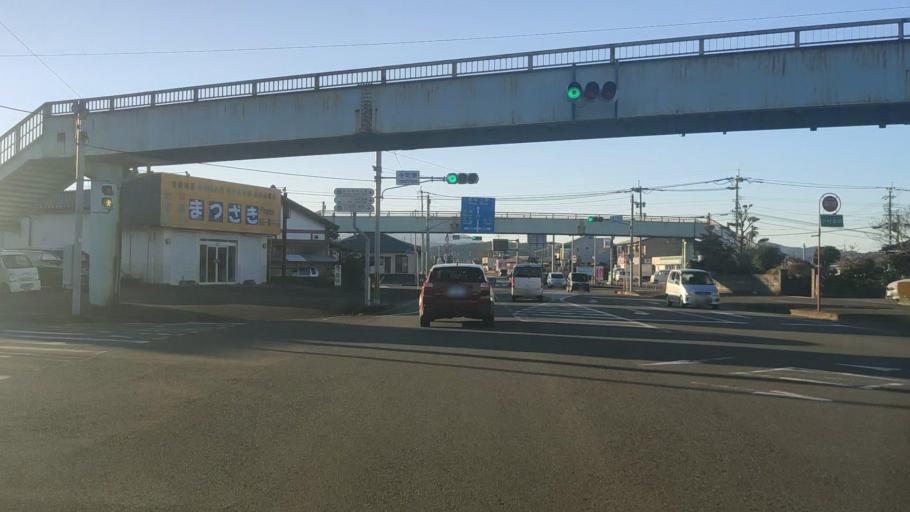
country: JP
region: Miyazaki
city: Miyazaki-shi
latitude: 31.8321
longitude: 131.2999
